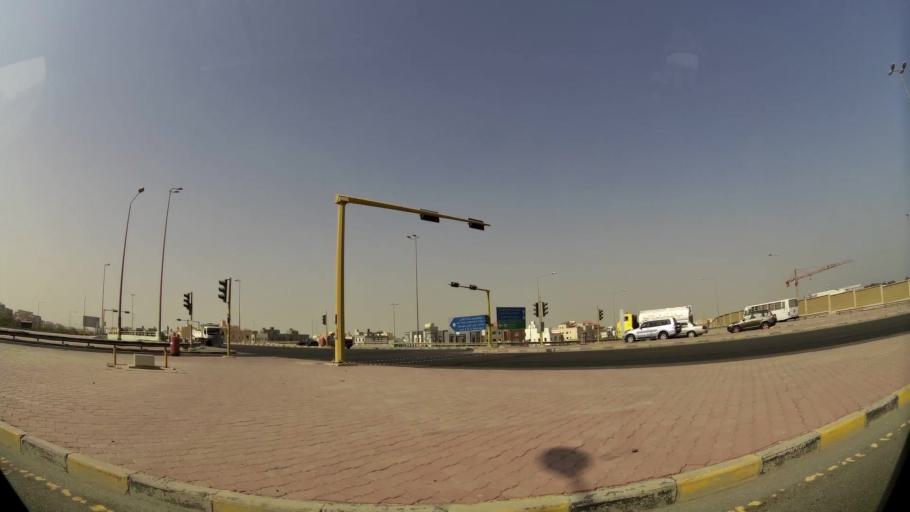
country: KW
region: Al Ahmadi
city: Al Fintas
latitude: 29.1841
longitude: 48.1129
